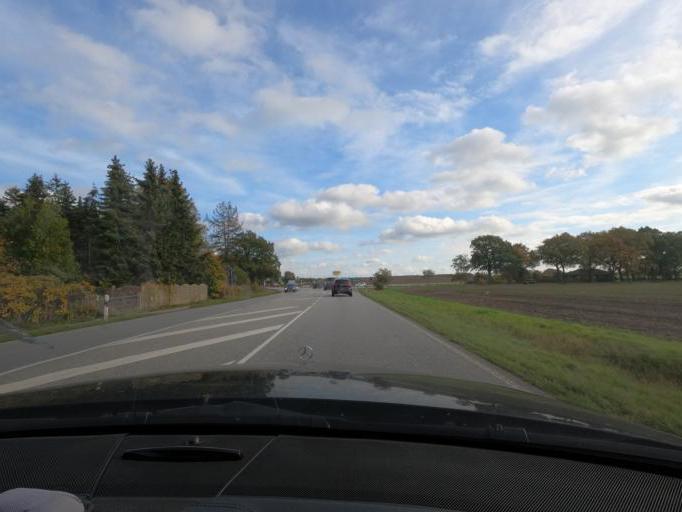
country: DE
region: Schleswig-Holstein
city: Hasenmoor
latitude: 53.8999
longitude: 9.9777
